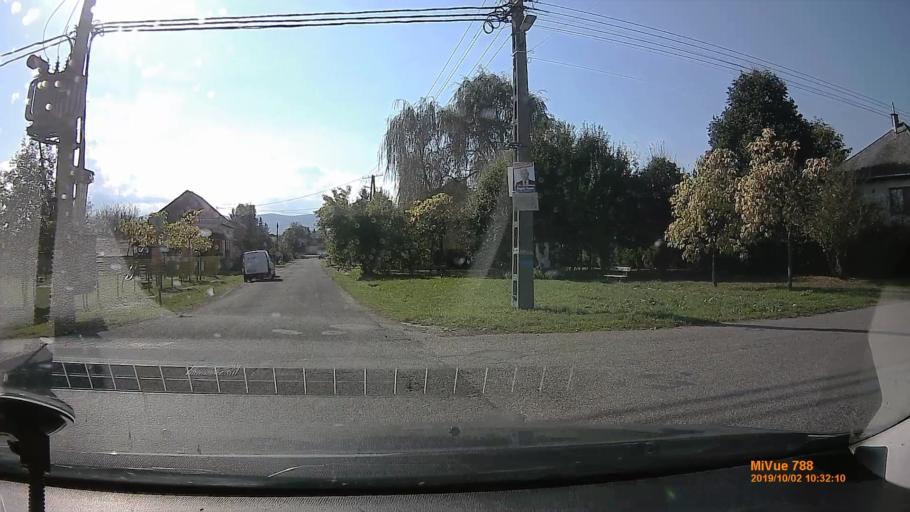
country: HU
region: Nograd
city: Batonyterenye
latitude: 48.0118
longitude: 19.8268
